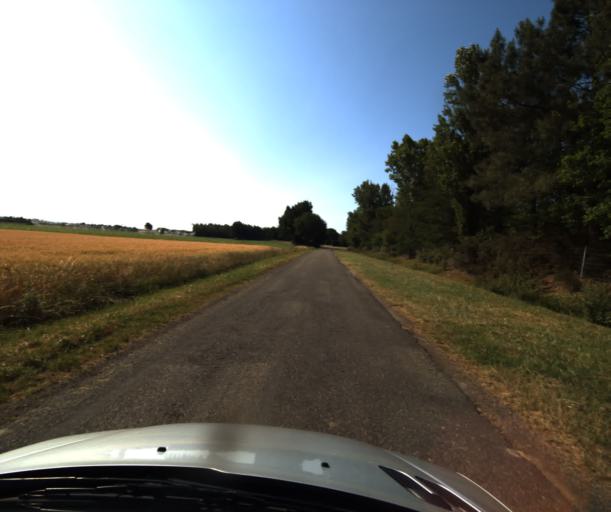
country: FR
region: Midi-Pyrenees
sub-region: Departement du Tarn-et-Garonne
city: Bressols
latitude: 43.9515
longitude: 1.2903
